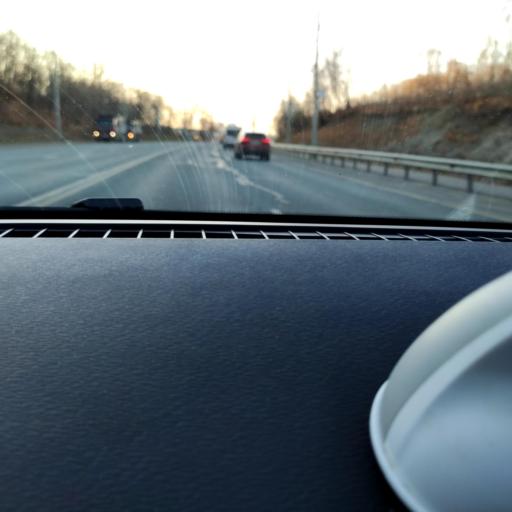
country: RU
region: Samara
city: Samara
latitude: 53.2819
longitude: 50.2287
